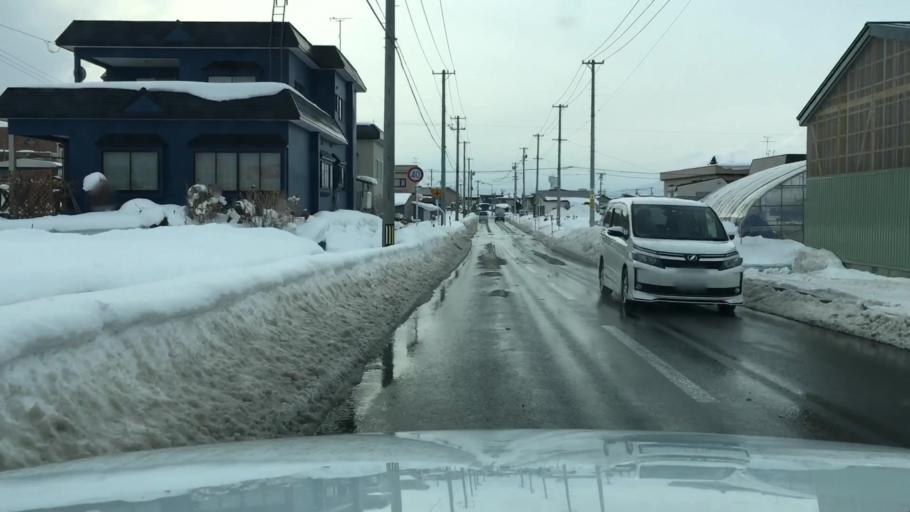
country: JP
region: Aomori
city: Kuroishi
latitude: 40.5919
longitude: 140.5657
